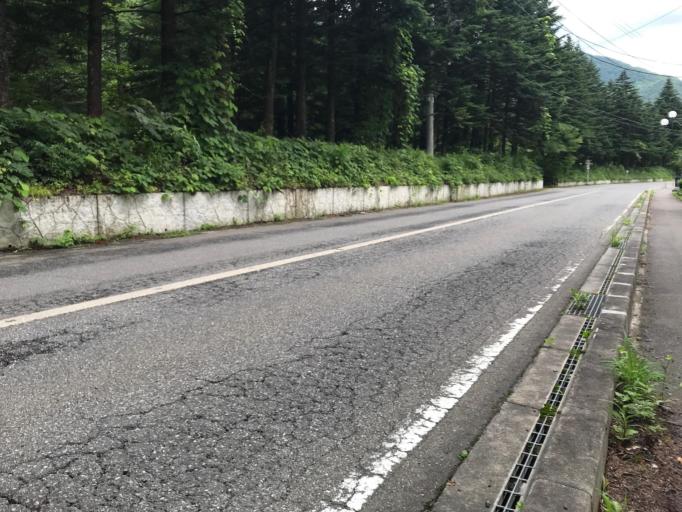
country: JP
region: Gunma
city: Numata
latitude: 36.8038
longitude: 138.9872
